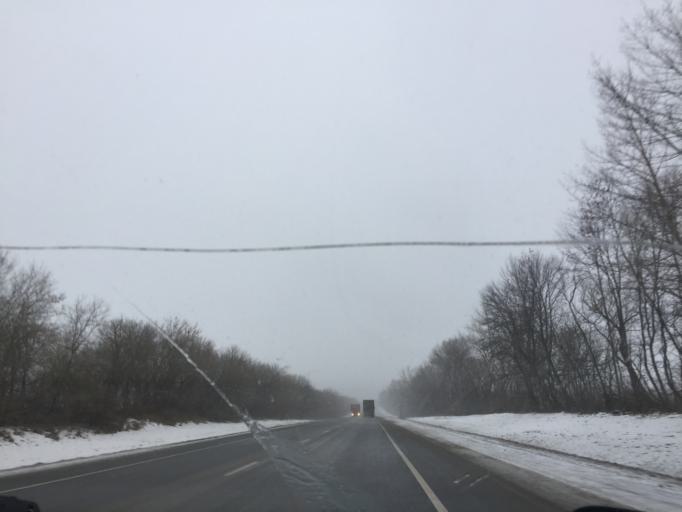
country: RU
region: Tula
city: Plavsk
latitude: 53.7679
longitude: 37.3456
